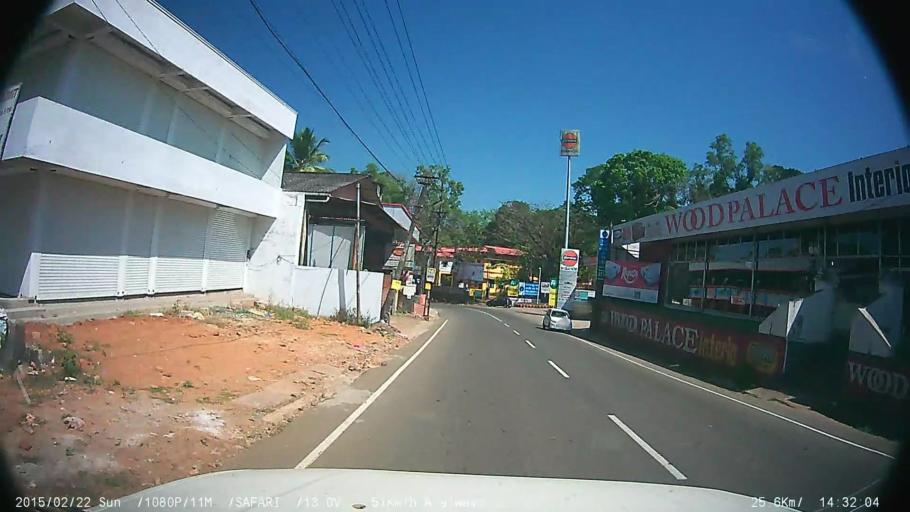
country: IN
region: Kerala
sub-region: Kottayam
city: Erattupetta
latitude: 9.5636
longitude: 76.7588
